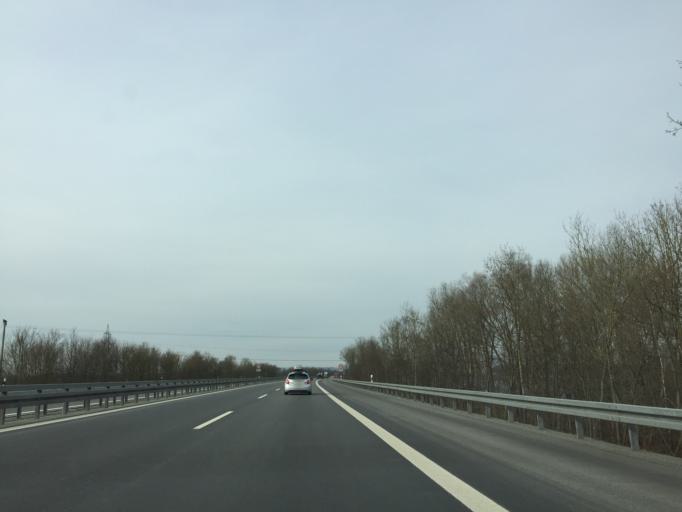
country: AT
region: Upper Austria
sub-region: Politischer Bezirk Scharding
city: Sankt Florian am Inn
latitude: 48.4171
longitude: 13.4086
